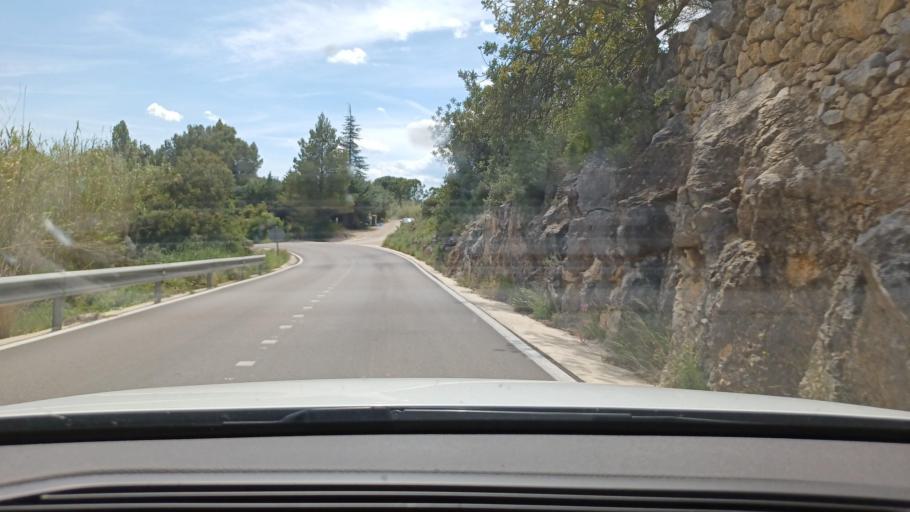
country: ES
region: Valencia
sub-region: Provincia de Castello
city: Rosell
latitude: 40.6485
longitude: 0.2688
